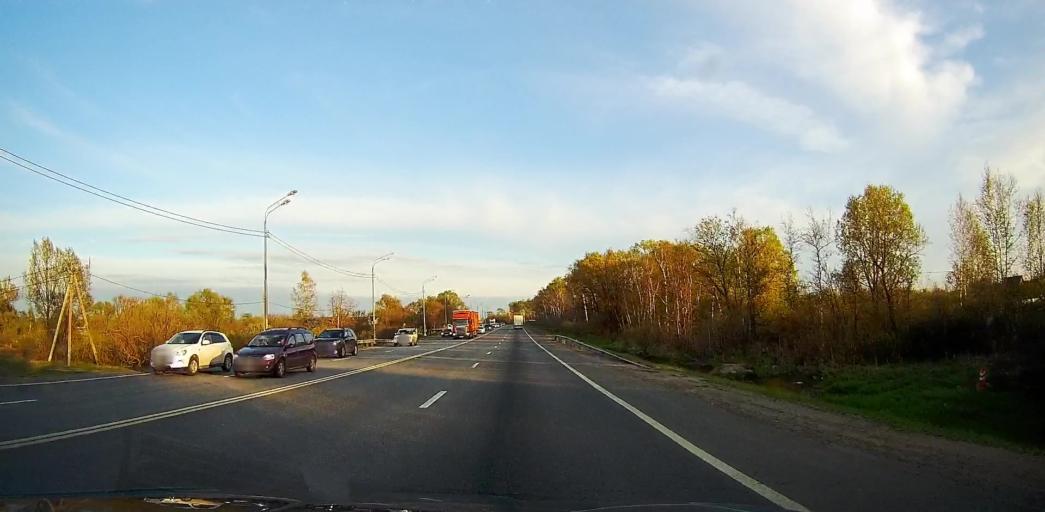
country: RU
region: Moskovskaya
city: Troitskoye
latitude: 55.2732
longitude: 38.4974
